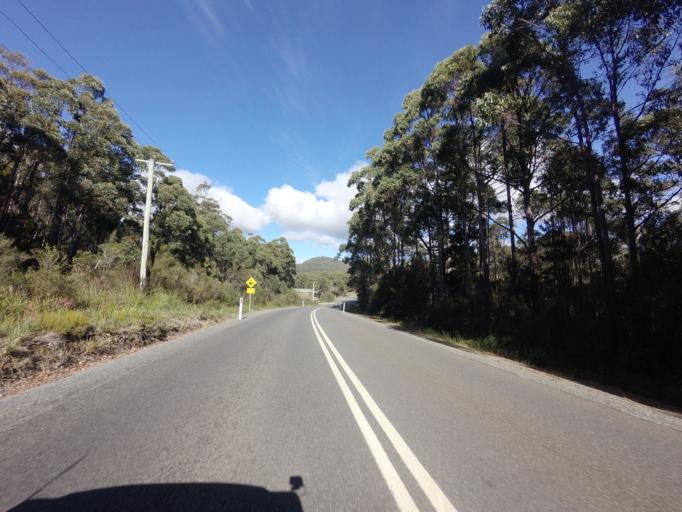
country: AU
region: Tasmania
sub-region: Clarence
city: Sandford
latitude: -43.0624
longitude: 147.8429
